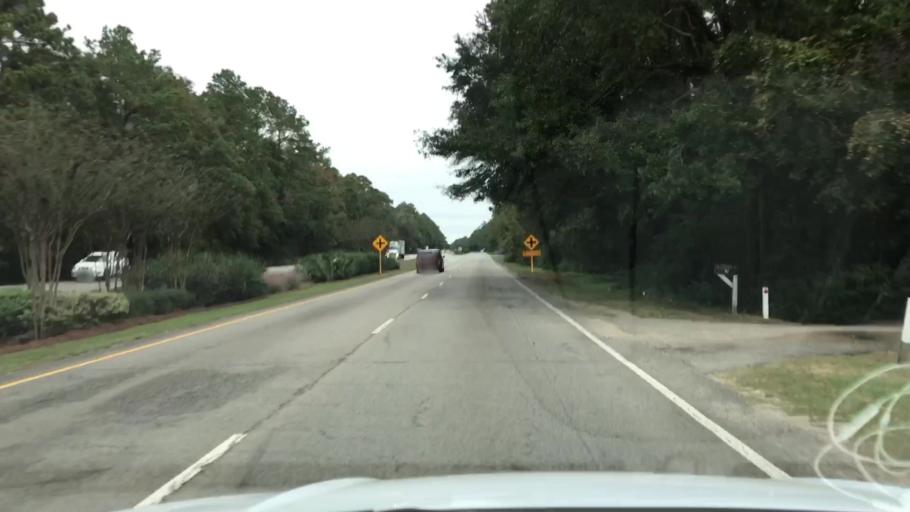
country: US
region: South Carolina
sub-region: Georgetown County
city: Murrells Inlet
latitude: 33.4943
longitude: -79.0877
